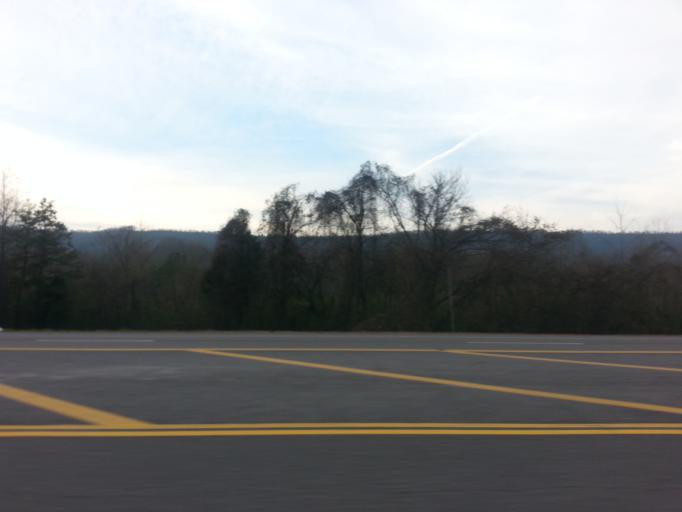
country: US
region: Tennessee
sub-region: Rhea County
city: Spring City
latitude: 35.6588
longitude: -84.8808
